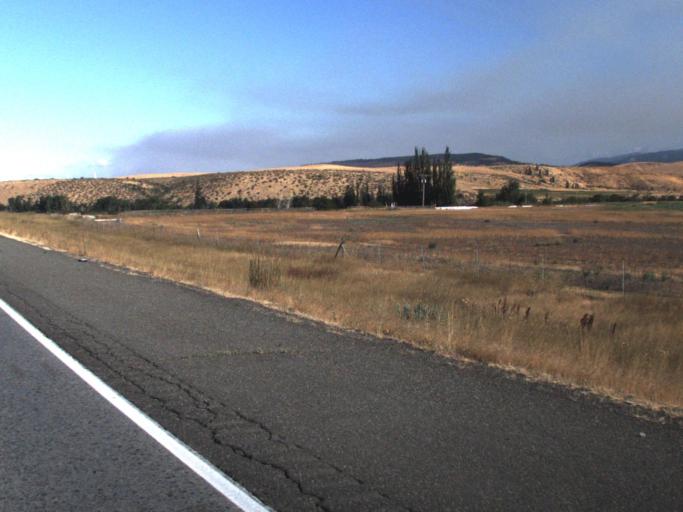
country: US
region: Washington
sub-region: Kittitas County
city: Ellensburg
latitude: 47.0755
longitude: -120.7177
